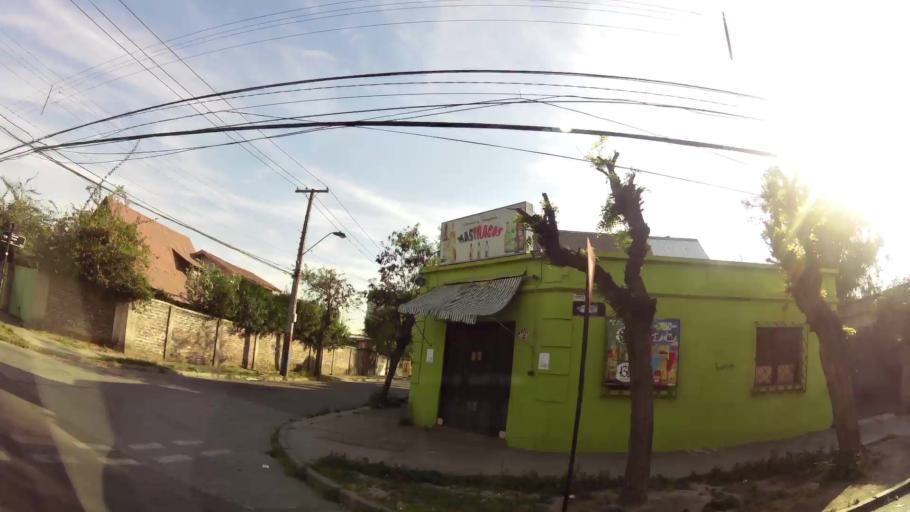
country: CL
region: Santiago Metropolitan
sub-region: Provincia de Santiago
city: Santiago
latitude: -33.5113
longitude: -70.6657
